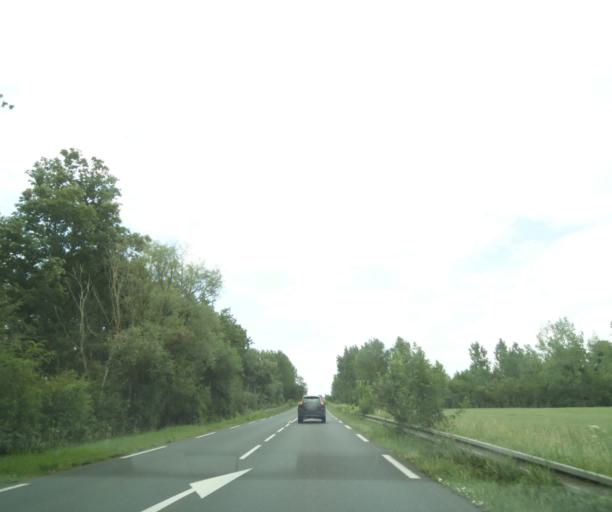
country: FR
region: Pays de la Loire
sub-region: Departement de Maine-et-Loire
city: Montreuil-Bellay
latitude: 47.1062
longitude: -0.1657
